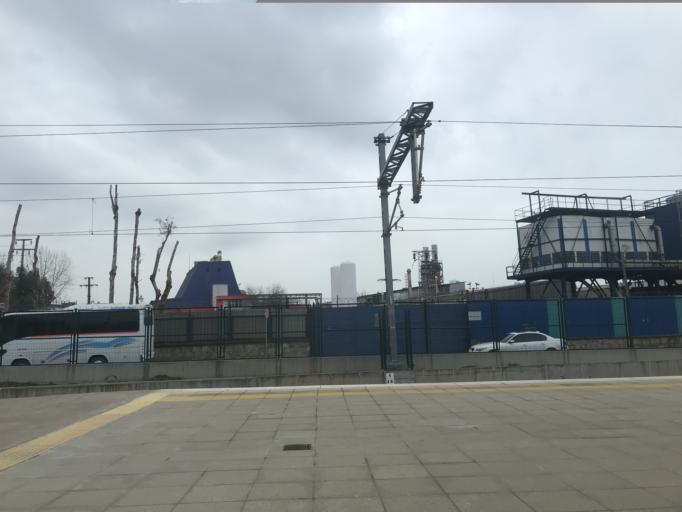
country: TR
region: Kocaeli
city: Darica
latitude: 40.7984
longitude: 29.3809
